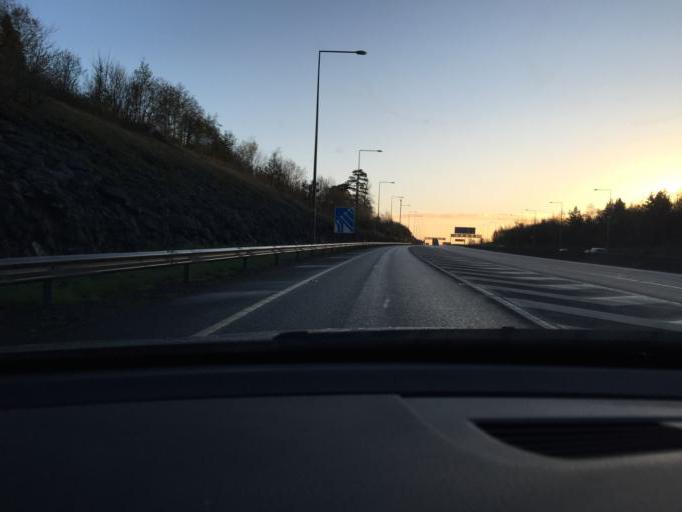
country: IE
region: Leinster
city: Castleknock
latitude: 53.3880
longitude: -6.3559
